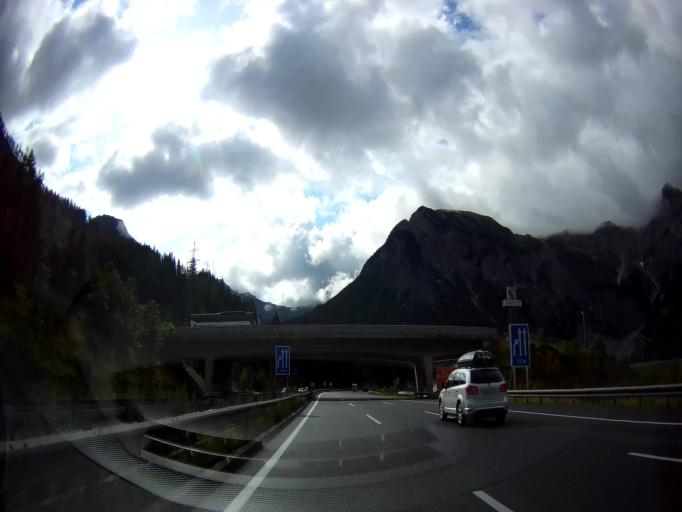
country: AT
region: Salzburg
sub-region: Politischer Bezirk Sankt Johann im Pongau
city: Untertauern
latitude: 47.2510
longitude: 13.4241
